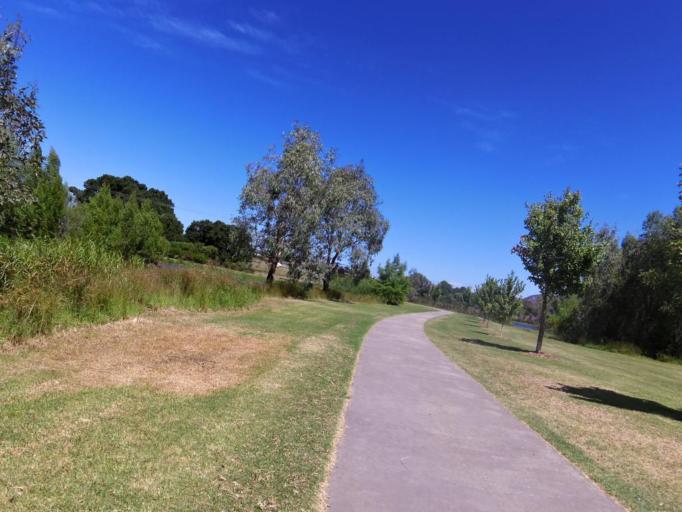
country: AU
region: Victoria
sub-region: Wodonga
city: Wodonga
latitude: -36.1131
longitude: 146.8874
